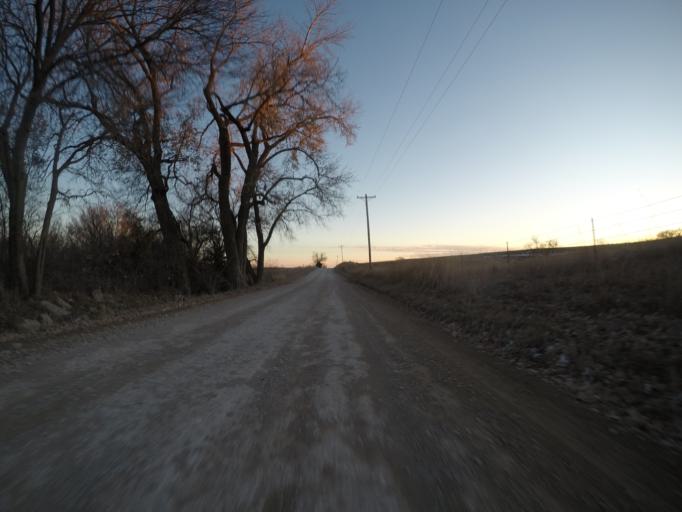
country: US
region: Kansas
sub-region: Riley County
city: Manhattan
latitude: 39.2589
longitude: -96.4826
